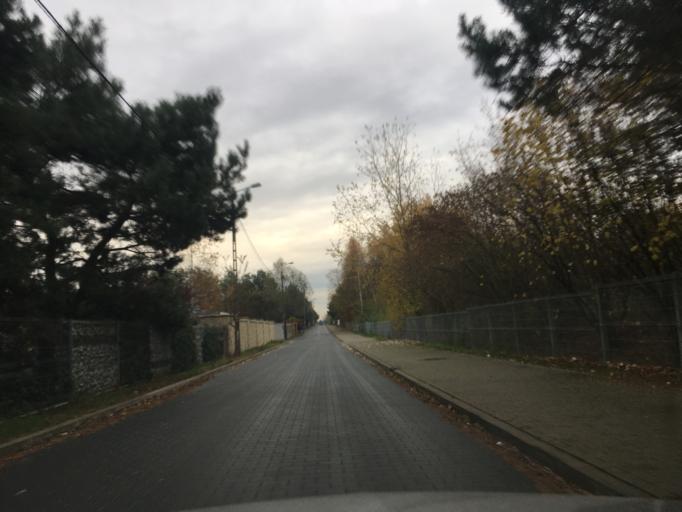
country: PL
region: Masovian Voivodeship
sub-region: Powiat piaseczynski
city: Lesznowola
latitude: 52.0749
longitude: 20.9183
